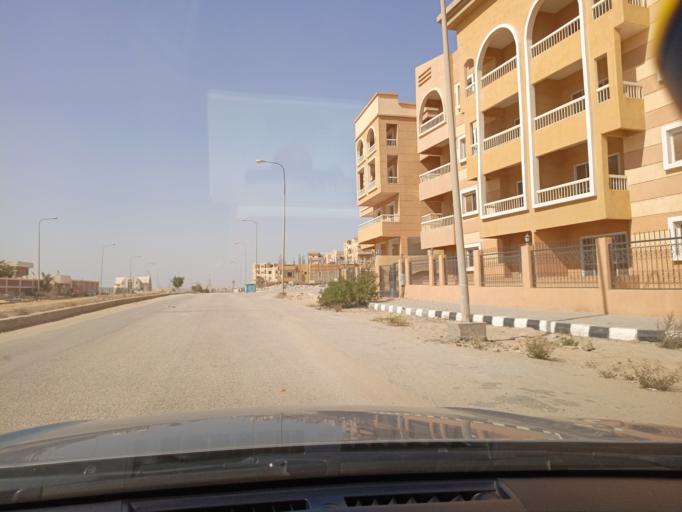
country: EG
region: Muhafazat al Qalyubiyah
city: Al Khankah
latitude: 30.2227
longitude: 31.4394
